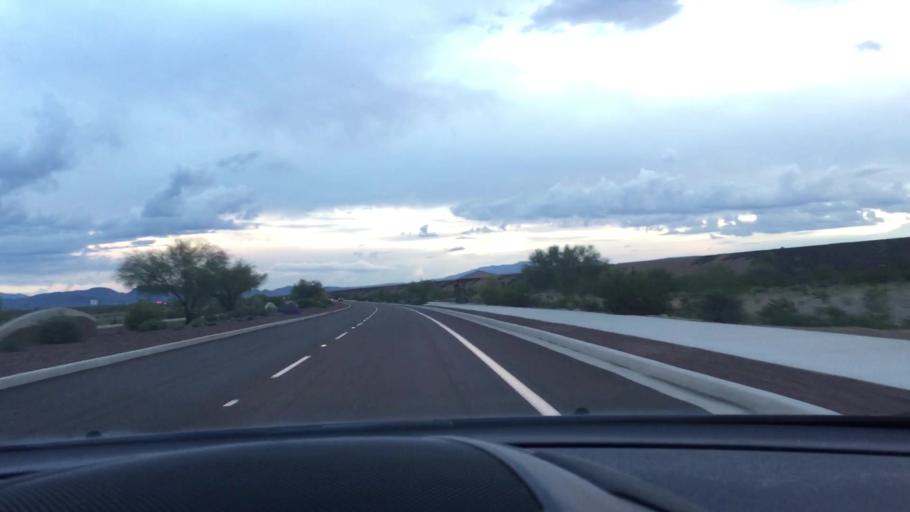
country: US
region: Arizona
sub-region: Maricopa County
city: Sun City West
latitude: 33.7493
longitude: -112.2549
